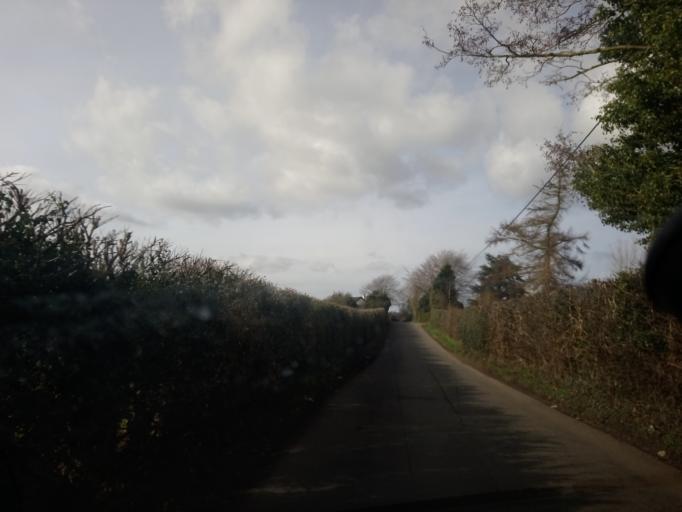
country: GB
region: England
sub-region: Shropshire
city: Stoke upon Tern
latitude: 52.7920
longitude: -2.5486
